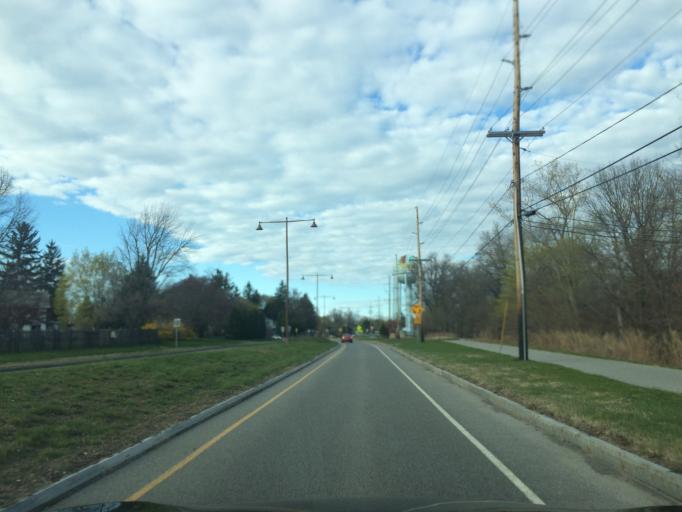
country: US
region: New York
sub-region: Monroe County
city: Irondequoit
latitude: 43.2148
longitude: -77.5479
